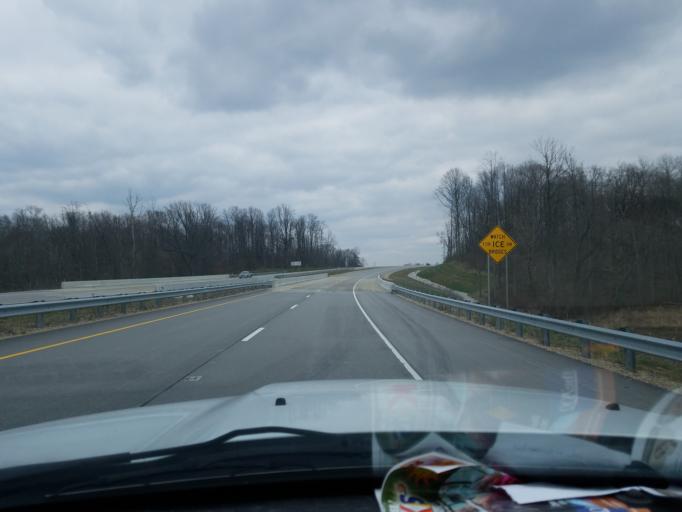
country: US
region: Indiana
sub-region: Vigo County
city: Terre Haute
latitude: 39.4100
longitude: -87.3617
